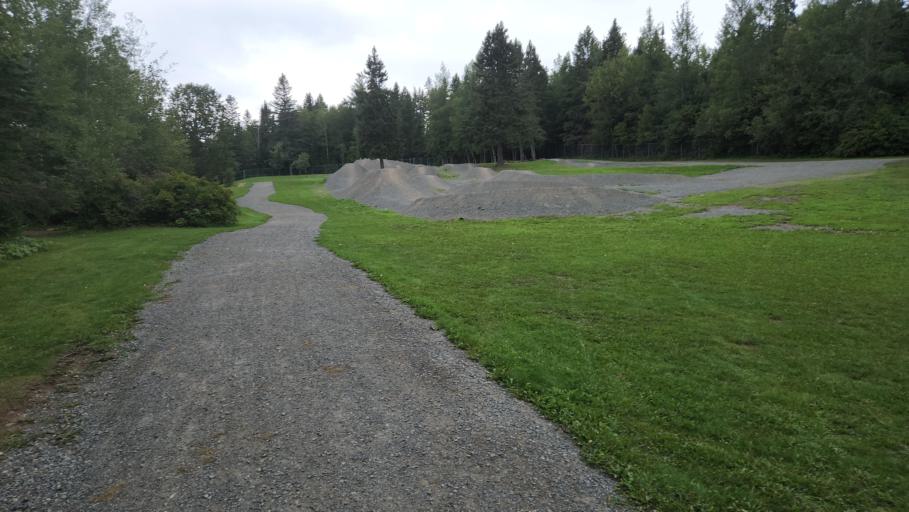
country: CA
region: Ontario
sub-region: Thunder Bay District
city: Thunder Bay
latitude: 48.4891
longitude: -89.1863
